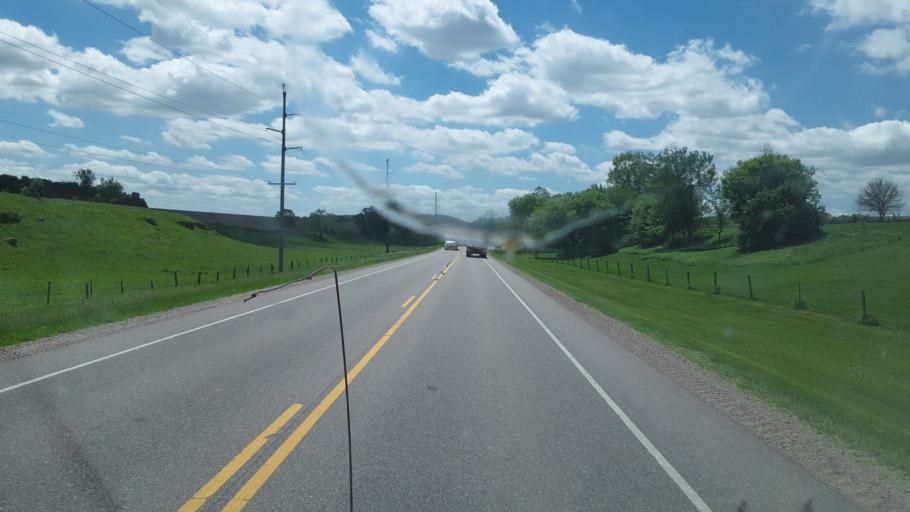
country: US
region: Wisconsin
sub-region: Sauk County
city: Reedsburg
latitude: 43.5770
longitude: -89.9603
